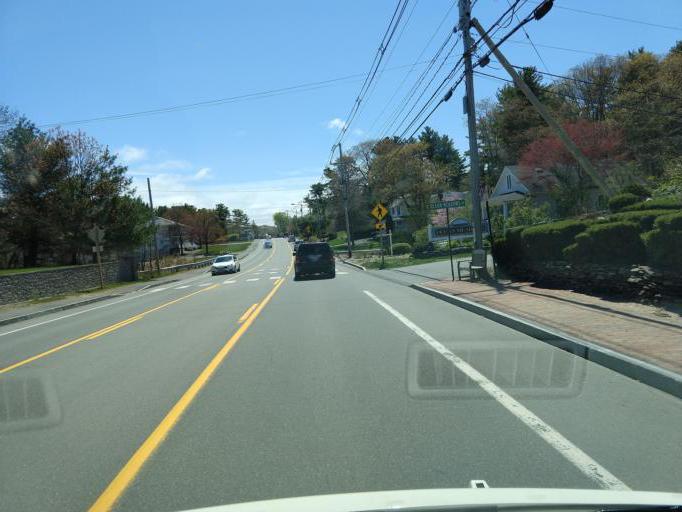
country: US
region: Maine
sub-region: York County
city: Ogunquit
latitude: 43.2614
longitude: -70.5987
